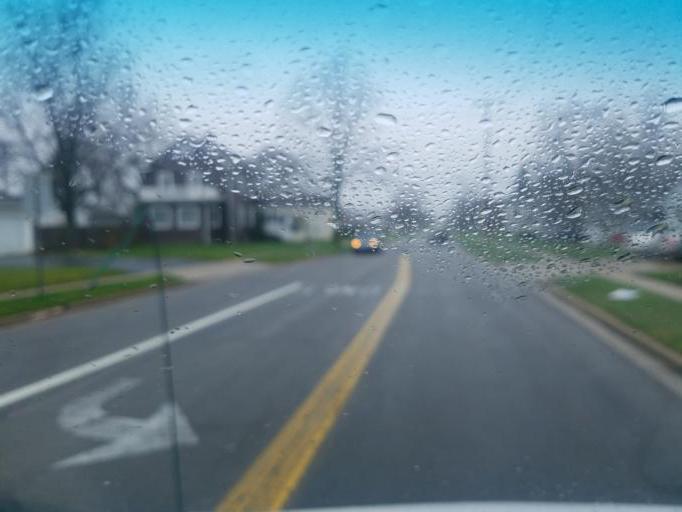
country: US
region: Ohio
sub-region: Hancock County
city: Findlay
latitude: 41.0661
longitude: -83.6502
